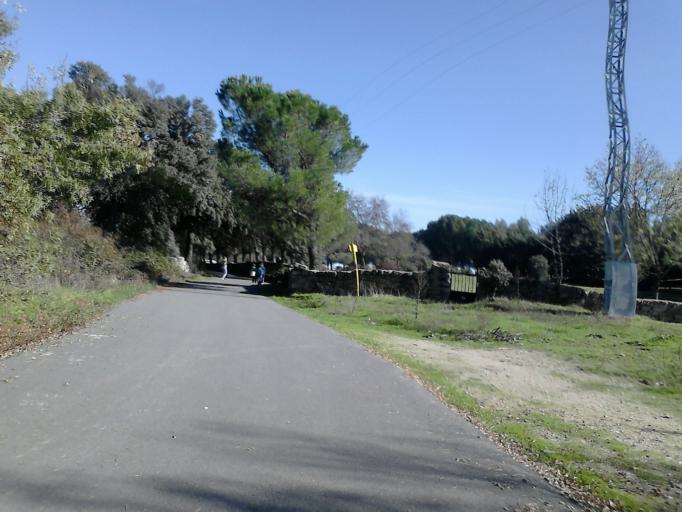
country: ES
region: Madrid
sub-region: Provincia de Madrid
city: Galapagar
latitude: 40.5741
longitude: -3.9887
